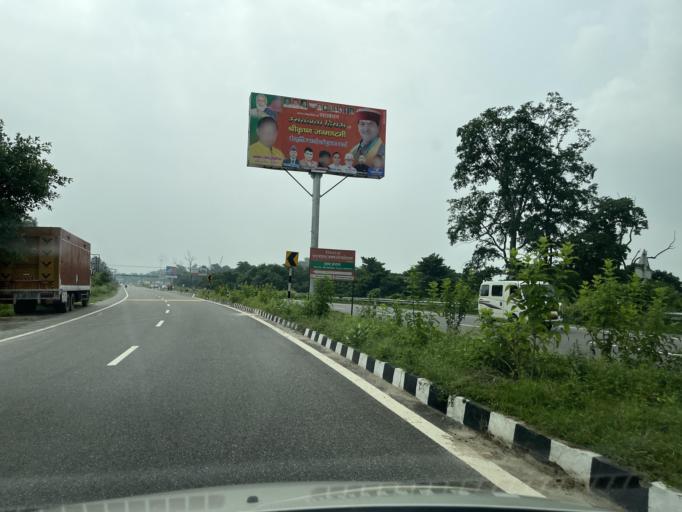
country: IN
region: Uttarakhand
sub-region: Dehradun
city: Raiwala
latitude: 30.0580
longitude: 78.2146
